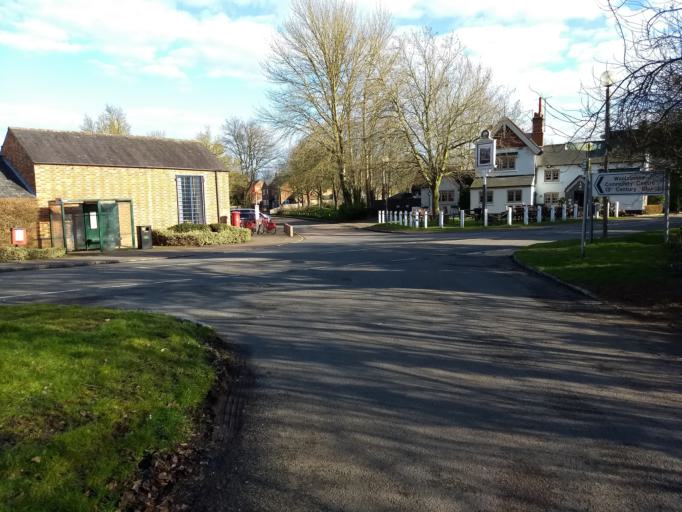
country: GB
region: England
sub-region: Milton Keynes
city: Milton Keynes
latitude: 52.0454
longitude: -0.7278
